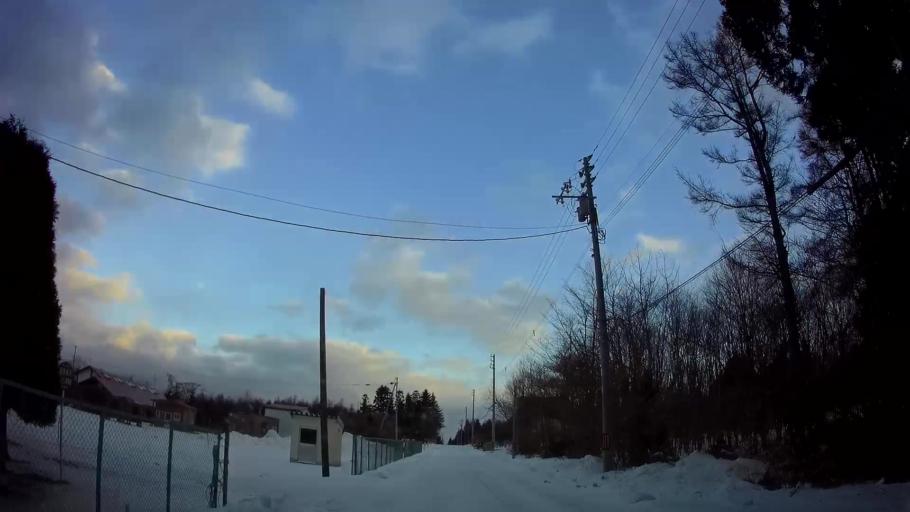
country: JP
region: Hokkaido
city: Nanae
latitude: 42.0224
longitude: 140.8342
